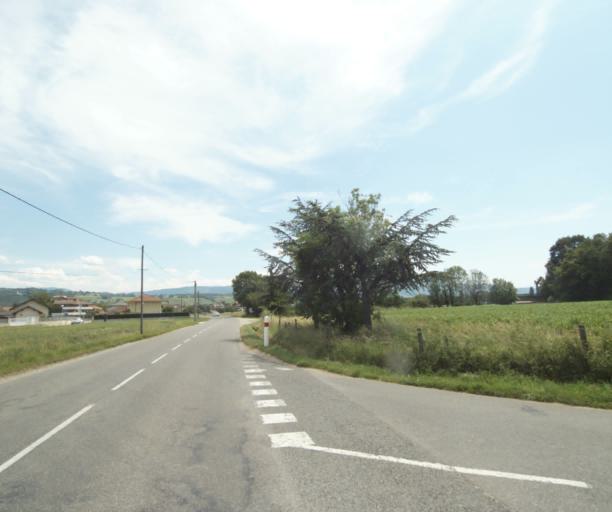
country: FR
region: Rhone-Alpes
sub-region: Departement de la Haute-Savoie
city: Douvaine
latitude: 46.3086
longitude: 6.2878
